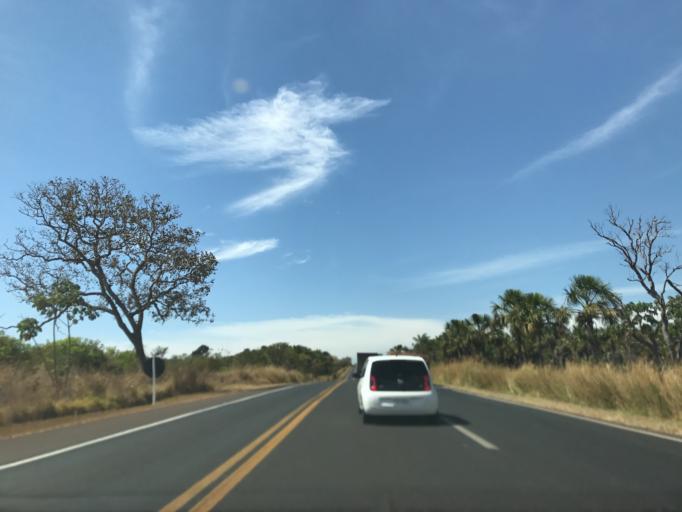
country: BR
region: Minas Gerais
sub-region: Prata
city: Prata
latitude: -19.0888
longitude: -48.9912
